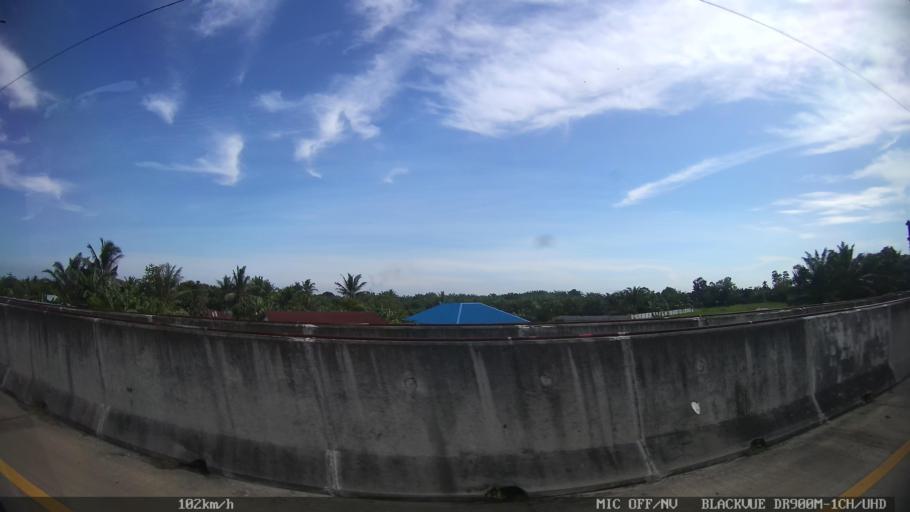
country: ID
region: North Sumatra
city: Sunggal
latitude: 3.6378
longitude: 98.5789
